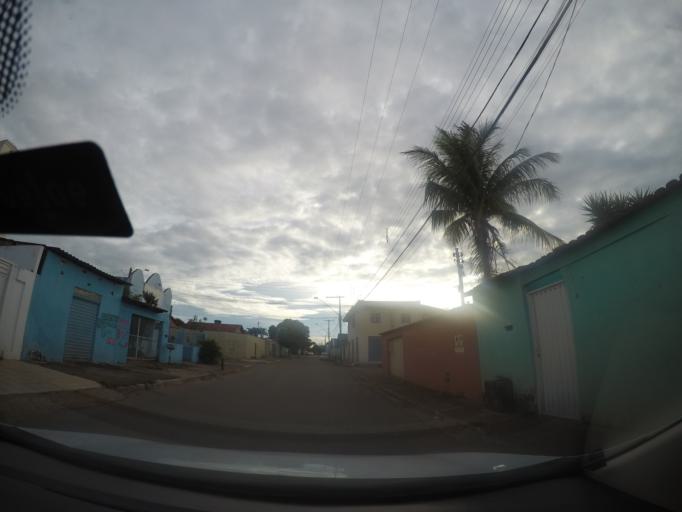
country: BR
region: Goias
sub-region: Goiania
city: Goiania
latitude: -16.6464
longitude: -49.3274
